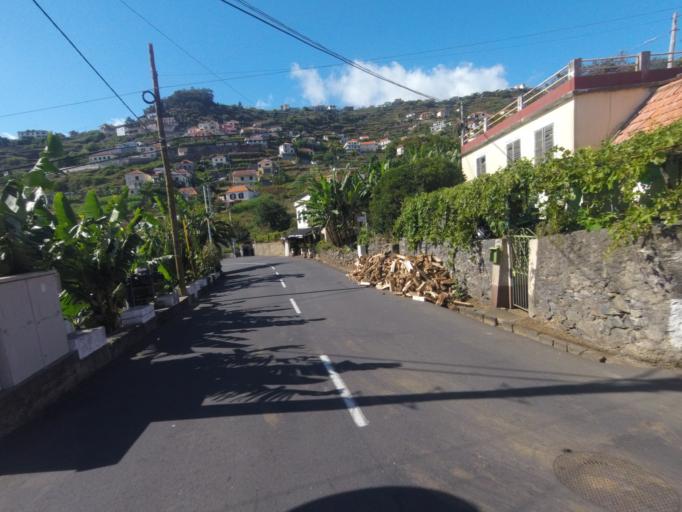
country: PT
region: Madeira
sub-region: Ribeira Brava
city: Campanario
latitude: 32.6745
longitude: -17.0263
